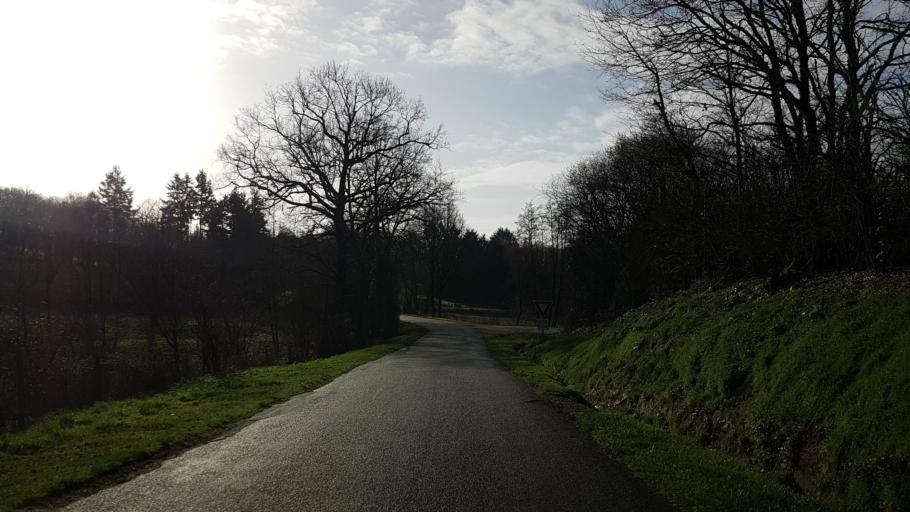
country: FR
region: Poitou-Charentes
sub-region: Departement de la Charente
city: Etagnac
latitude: 45.8901
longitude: 0.7741
